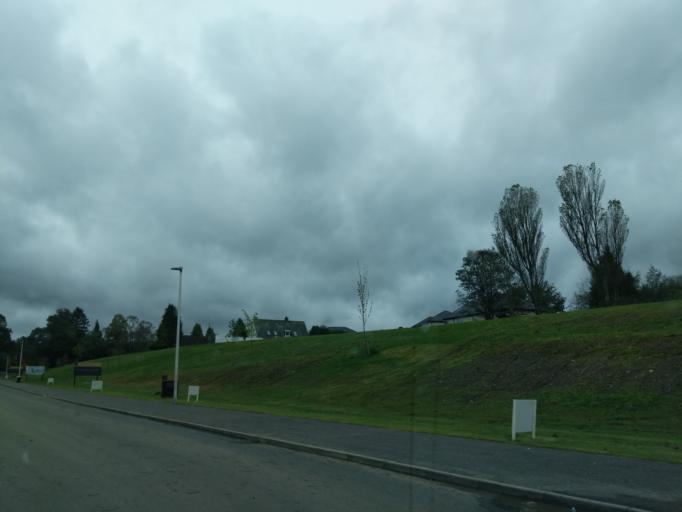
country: GB
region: Scotland
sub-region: Edinburgh
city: Balerno
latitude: 55.8906
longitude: -3.3369
